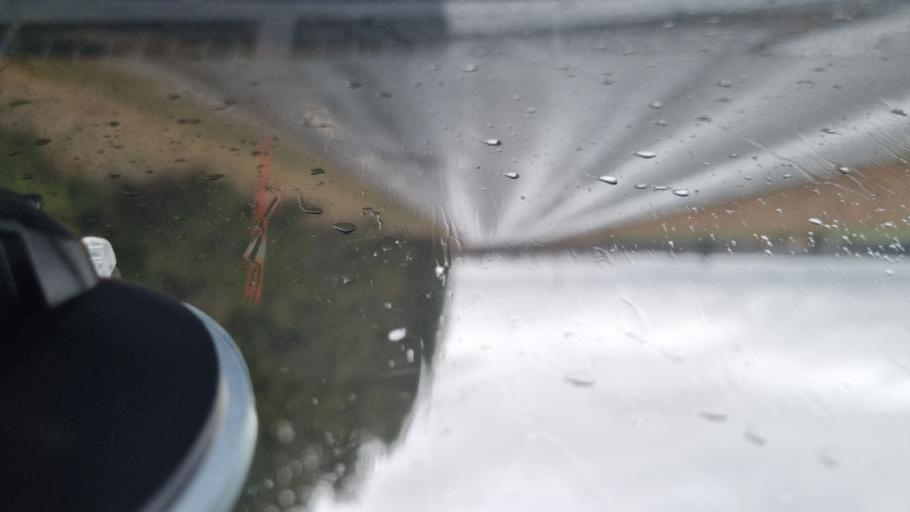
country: SE
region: Stockholm
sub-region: Sigtuna Kommun
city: Sigtuna
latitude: 59.5844
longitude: 17.6662
